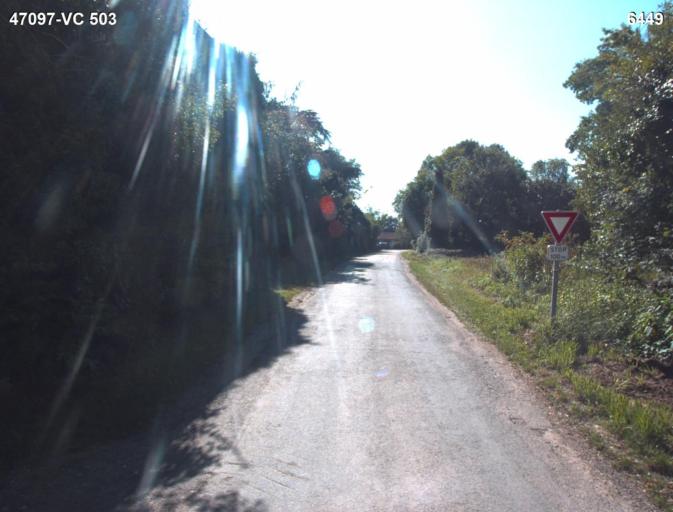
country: FR
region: Aquitaine
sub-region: Departement du Lot-et-Garonne
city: Port-Sainte-Marie
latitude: 44.2394
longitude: 0.3843
